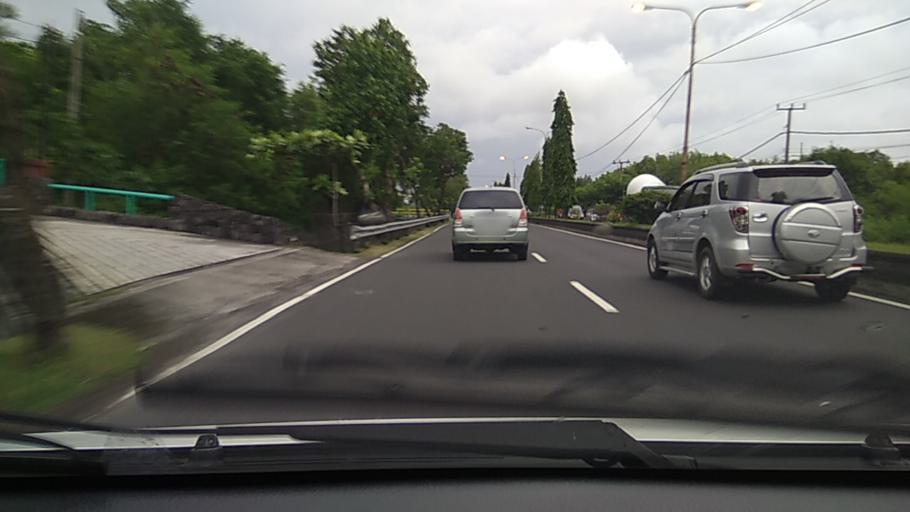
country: ID
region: Bali
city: Karyadharma
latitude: -8.7110
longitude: 115.2341
